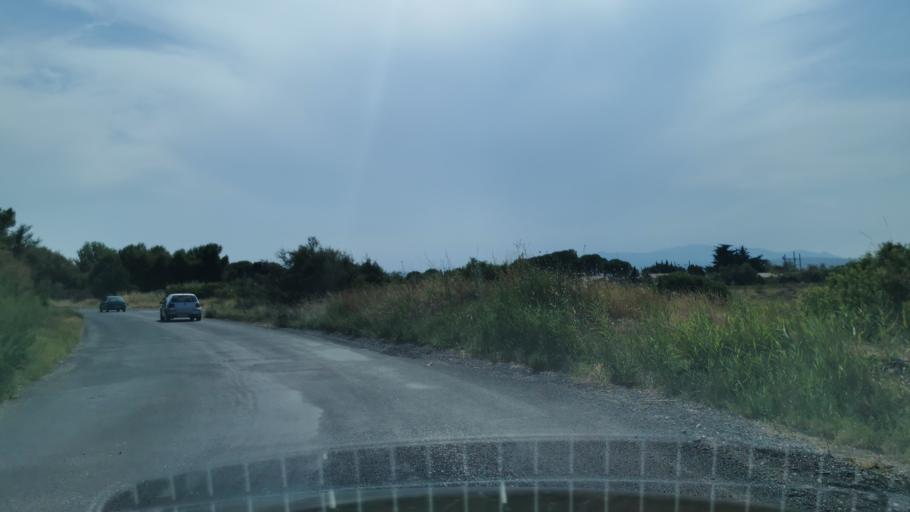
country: FR
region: Languedoc-Roussillon
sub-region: Departement de l'Aude
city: Leucate
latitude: 42.9362
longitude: 3.0184
